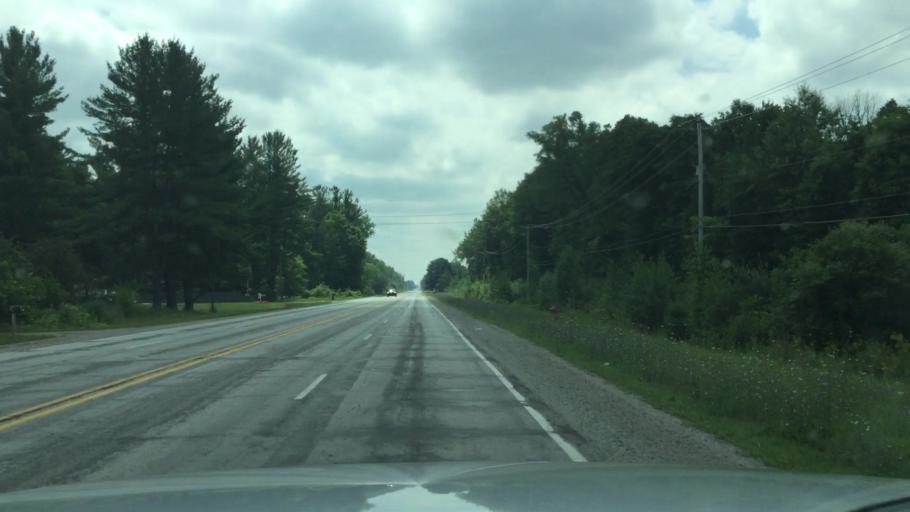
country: US
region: Michigan
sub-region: Saginaw County
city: Birch Run
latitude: 43.2873
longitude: -83.7975
